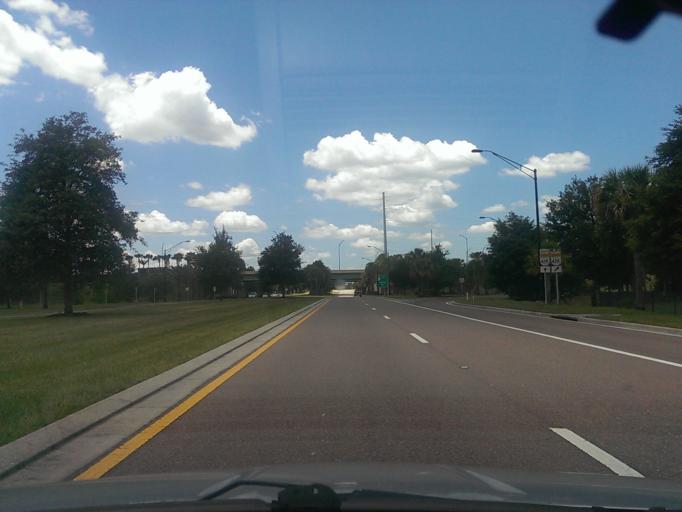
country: US
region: Florida
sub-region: Polk County
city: Citrus Ridge
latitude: 28.3783
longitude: -81.6090
